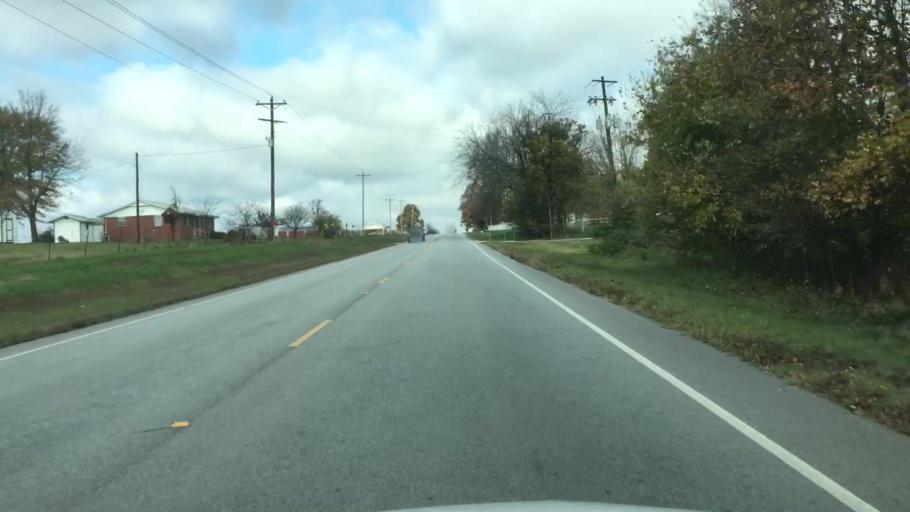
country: US
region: Arkansas
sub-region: Benton County
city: Centerton
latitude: 36.2662
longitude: -94.3504
